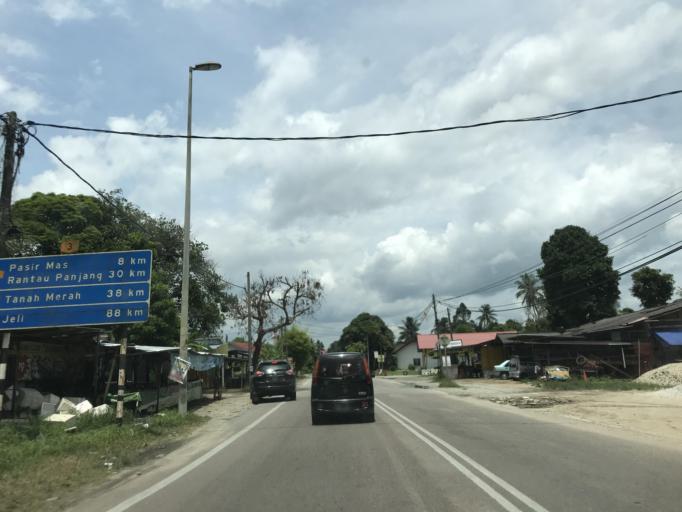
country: MY
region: Kelantan
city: Pasir Mas
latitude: 6.0631
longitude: 102.2044
